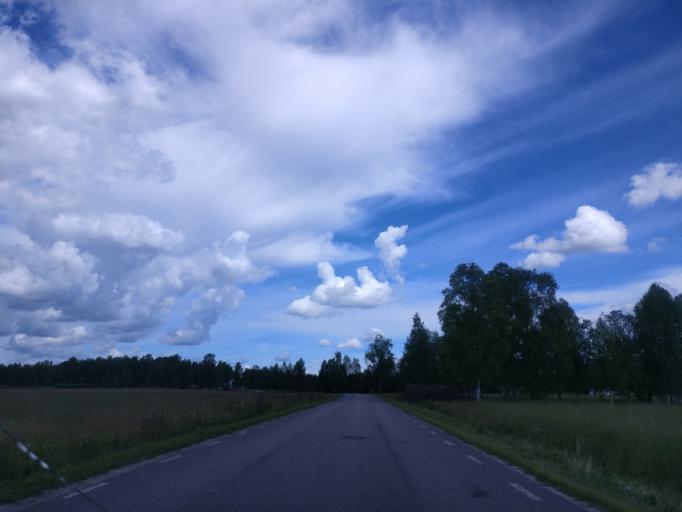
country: SE
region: Vaermland
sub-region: Hagfors Kommun
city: Ekshaerad
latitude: 60.1279
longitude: 13.4569
